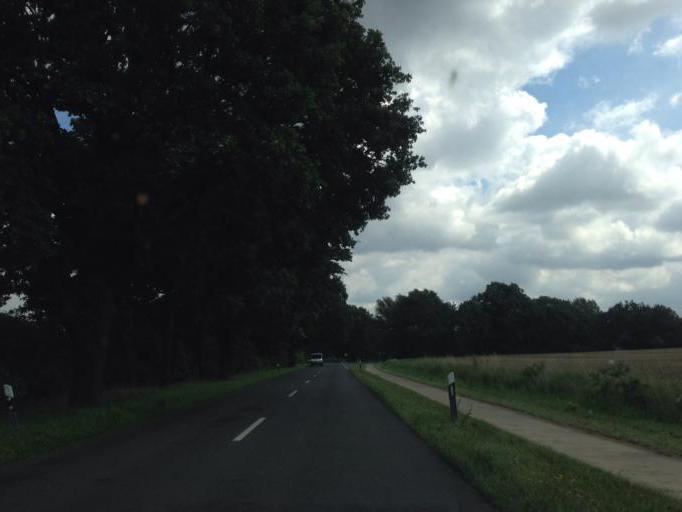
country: DE
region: Lower Saxony
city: Adendorf
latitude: 53.2977
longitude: 10.4358
